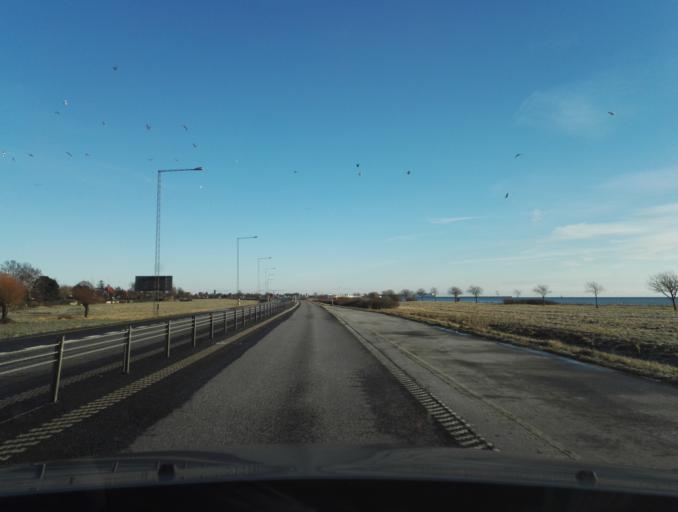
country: SE
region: Skane
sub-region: Trelleborgs Kommun
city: Skare
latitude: 55.3766
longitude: 13.1017
